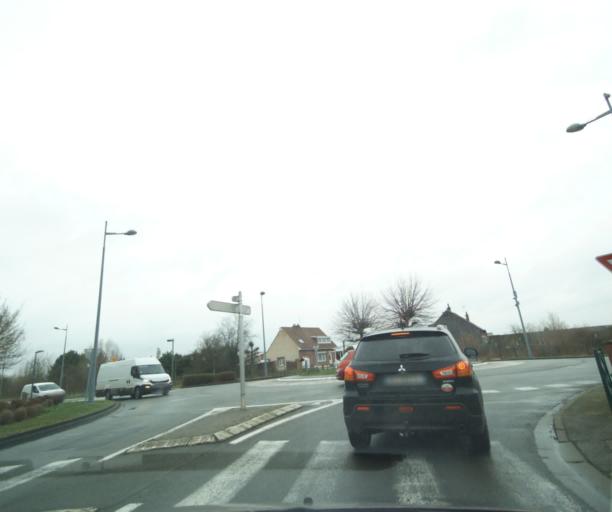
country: FR
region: Nord-Pas-de-Calais
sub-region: Departement du Nord
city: Prouvy
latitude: 50.3253
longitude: 3.4521
